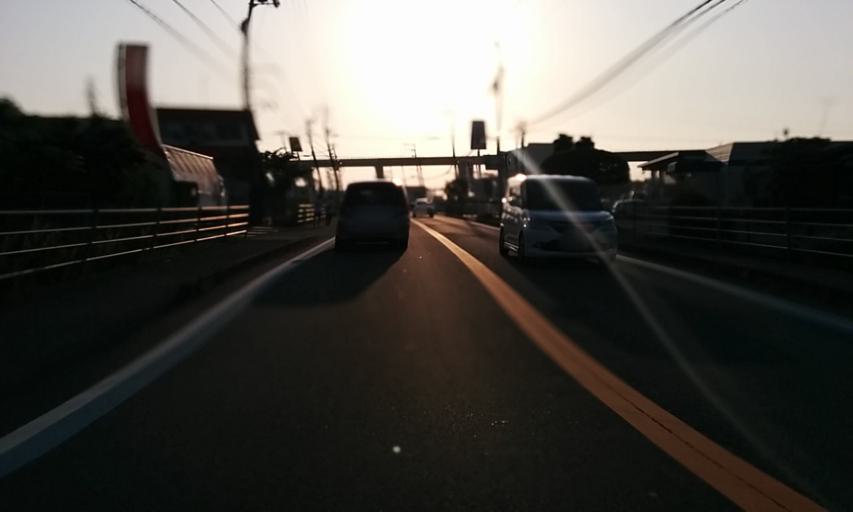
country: JP
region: Ehime
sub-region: Shikoku-chuo Shi
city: Matsuyama
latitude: 33.7895
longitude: 132.7753
